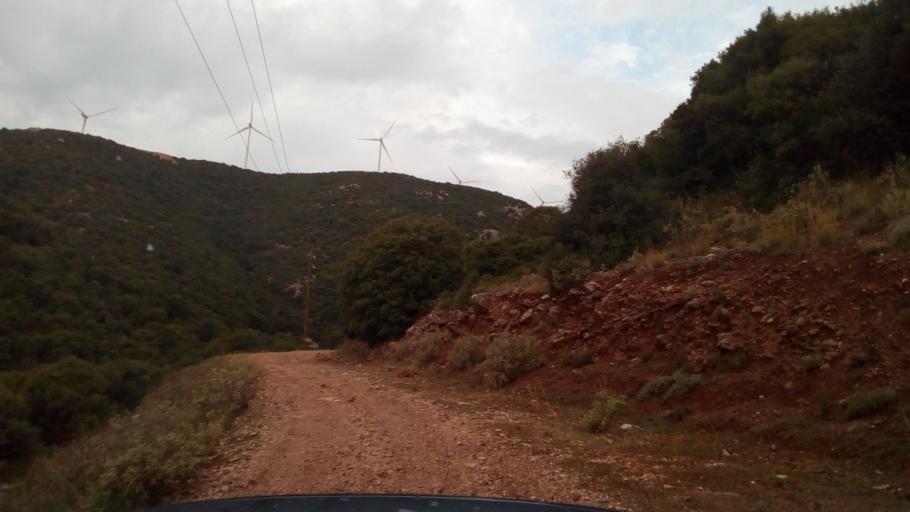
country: GR
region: West Greece
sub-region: Nomos Achaias
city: Kamarai
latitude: 38.4136
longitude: 22.0518
